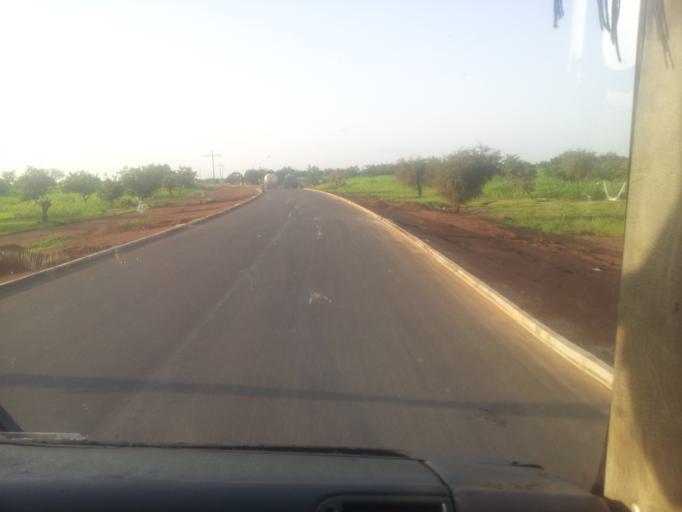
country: BF
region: Centre-Est
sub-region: Kouritenga Province
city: Koupela
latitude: 12.0145
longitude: -0.3613
